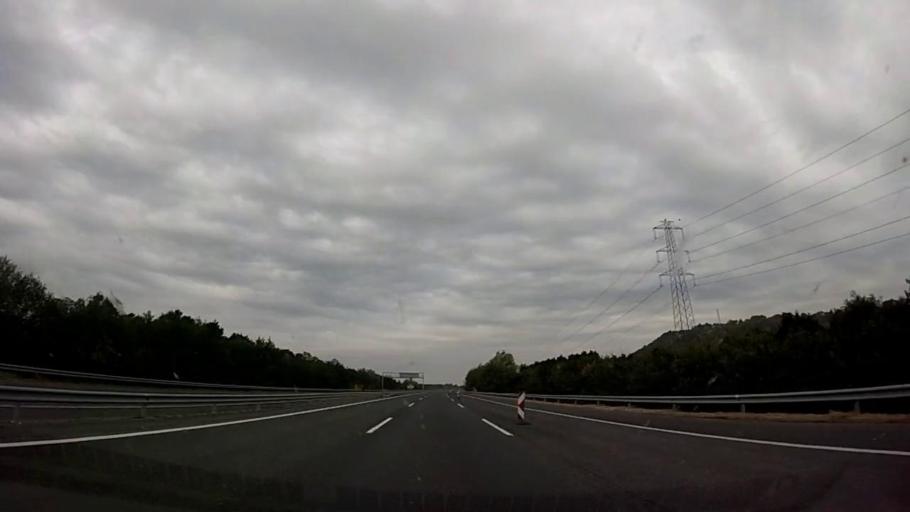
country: HR
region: Medimurska
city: Podturen
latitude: 46.5124
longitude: 16.5463
